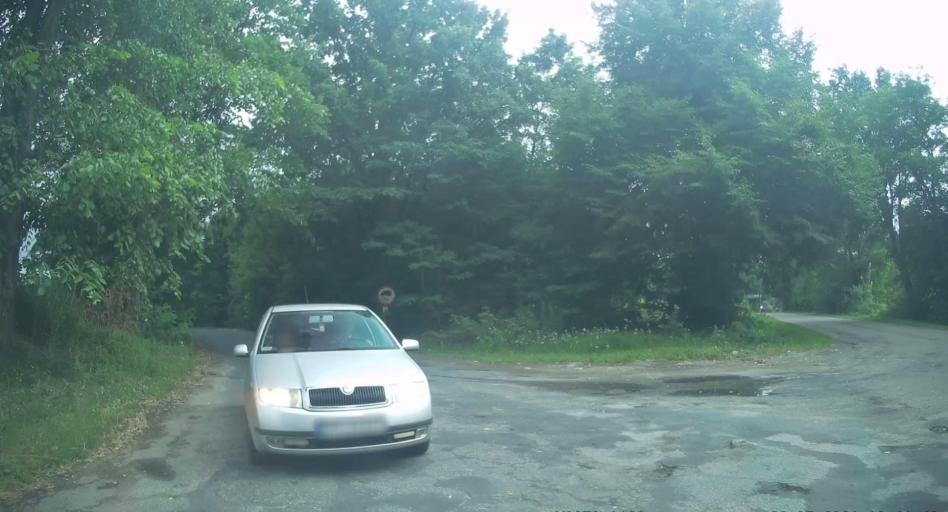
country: PL
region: Lodz Voivodeship
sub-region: Powiat rawski
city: Rawa Mazowiecka
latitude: 51.7448
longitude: 20.1854
